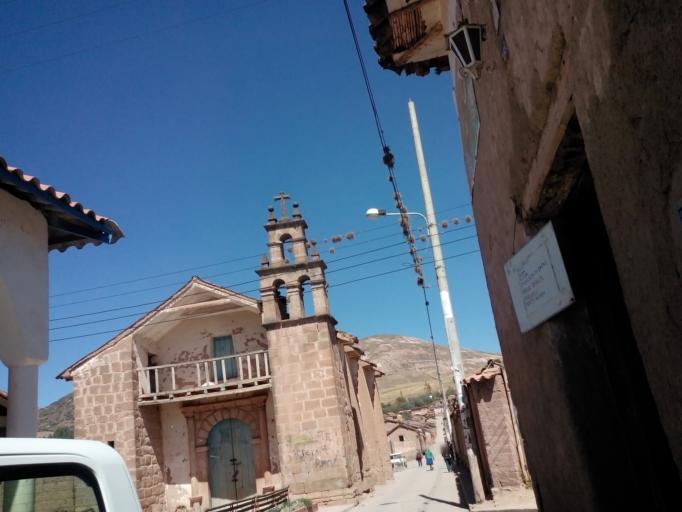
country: PE
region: Cusco
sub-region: Provincia de Urubamba
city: Maras
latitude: -13.3349
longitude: -72.1562
